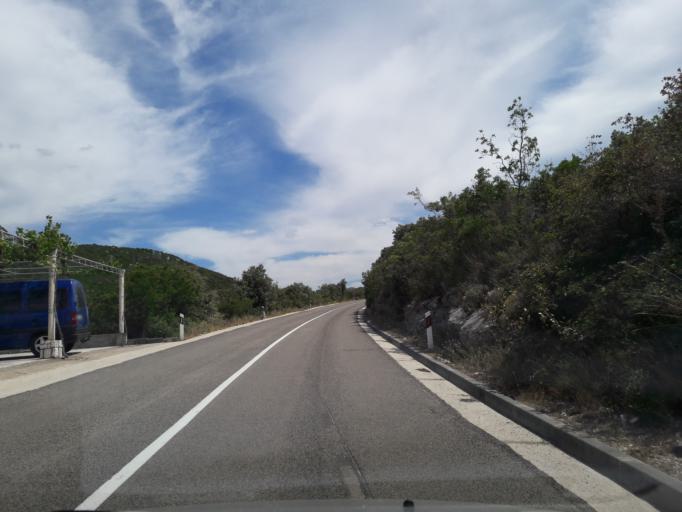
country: HR
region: Dubrovacko-Neretvanska
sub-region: Grad Dubrovnik
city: Opuzen
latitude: 42.9136
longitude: 17.4753
